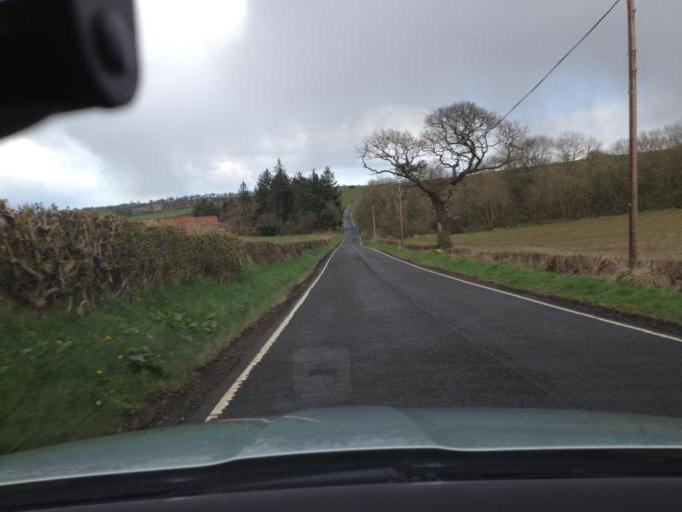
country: GB
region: Scotland
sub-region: West Lothian
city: Linlithgow
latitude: 55.9622
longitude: -3.5876
